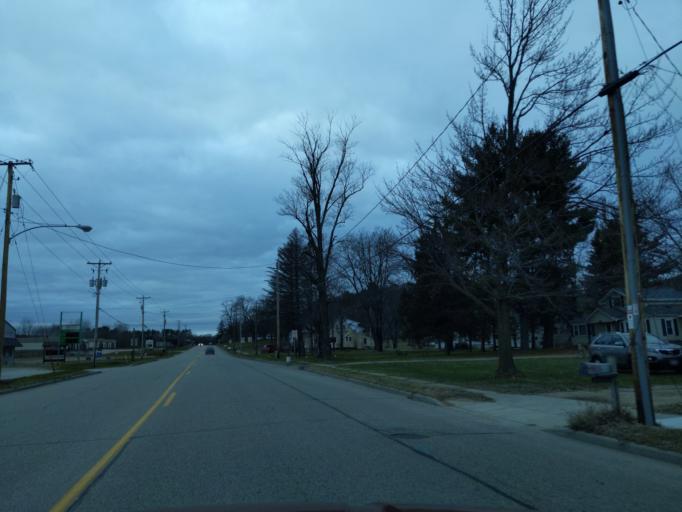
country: US
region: Wisconsin
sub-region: Waushara County
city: Wautoma
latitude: 44.0766
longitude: -89.2962
